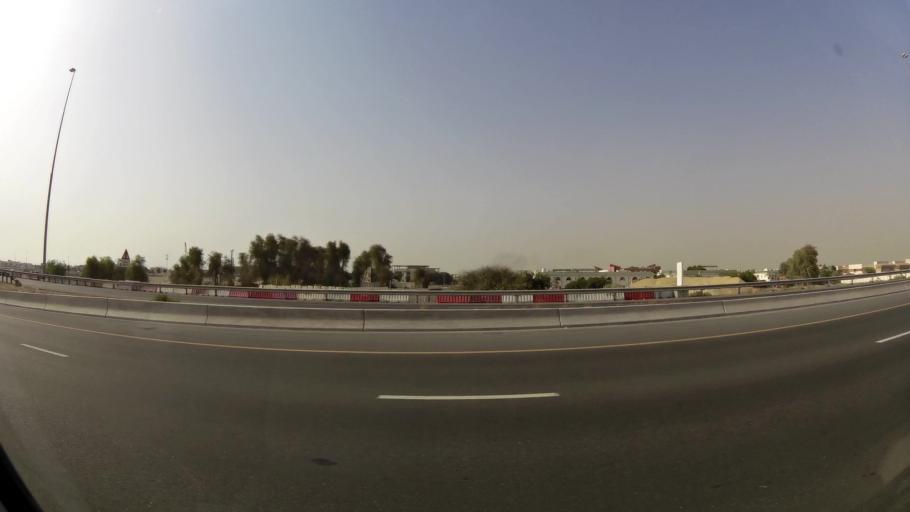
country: AE
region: Ash Shariqah
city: Sharjah
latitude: 25.2344
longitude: 55.4283
